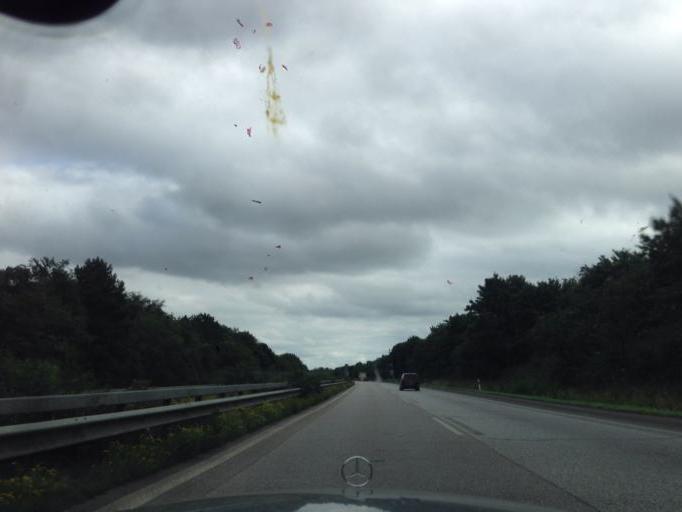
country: DE
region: Schleswig-Holstein
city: Eisendorf
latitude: 54.2044
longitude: 9.8740
